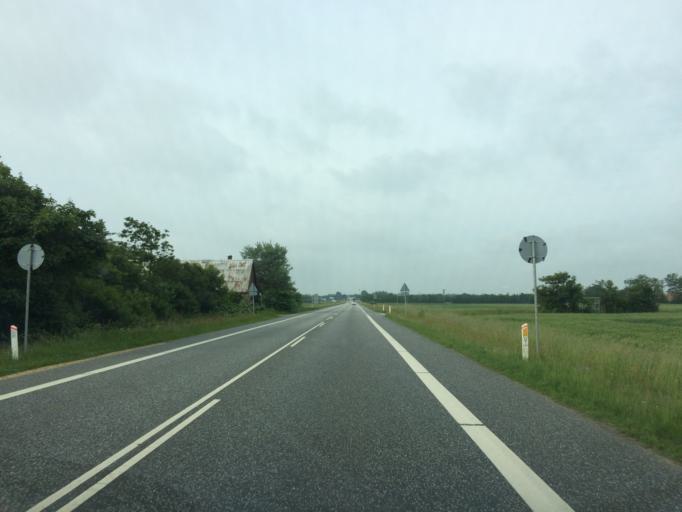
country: DK
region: Central Jutland
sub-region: Holstebro Kommune
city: Ulfborg
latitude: 56.2894
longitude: 8.3369
